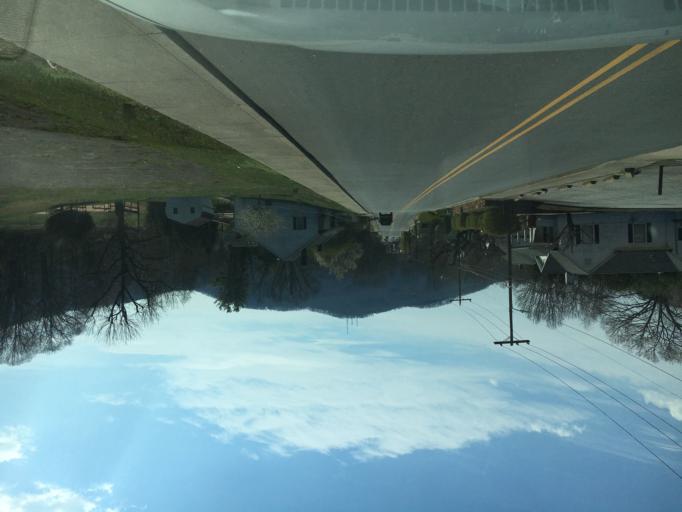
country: US
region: North Carolina
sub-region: McDowell County
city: Marion
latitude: 35.6843
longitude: -81.9919
